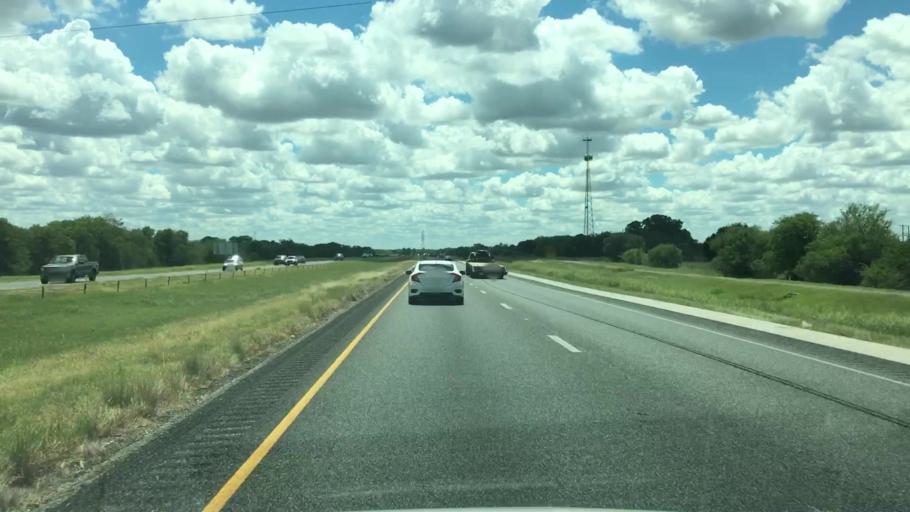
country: US
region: Texas
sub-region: Bexar County
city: Elmendorf
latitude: 29.2626
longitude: -98.3956
